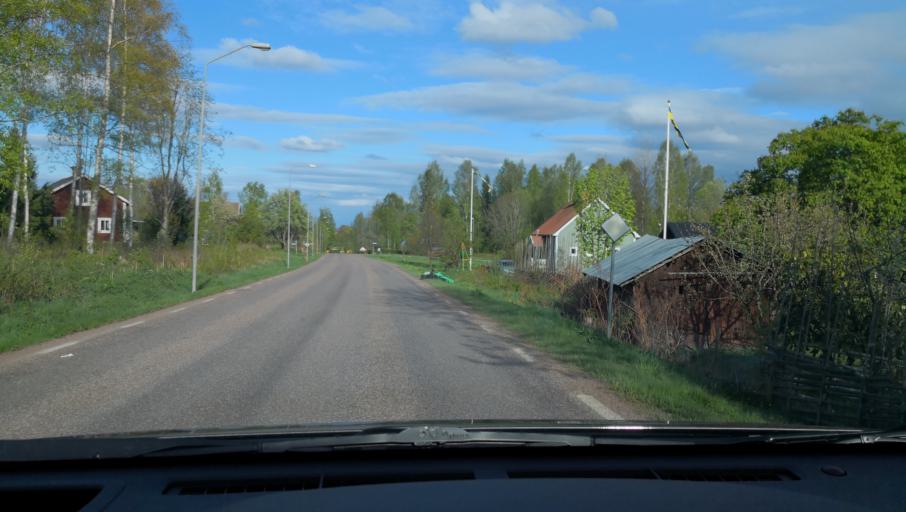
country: SE
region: Dalarna
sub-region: Saters Kommun
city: Saeter
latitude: 60.2992
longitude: 15.8419
